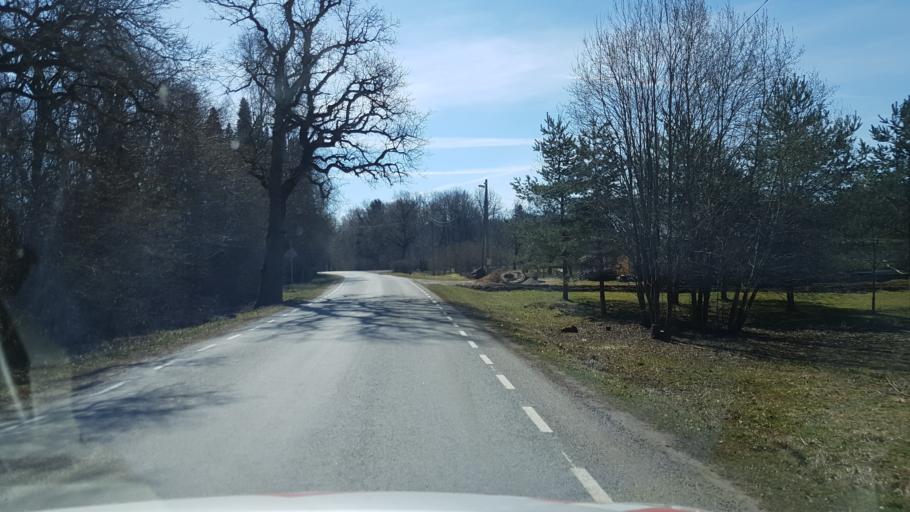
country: EE
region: Laeaene-Virumaa
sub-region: Vinni vald
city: Vinni
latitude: 59.2893
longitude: 26.4268
